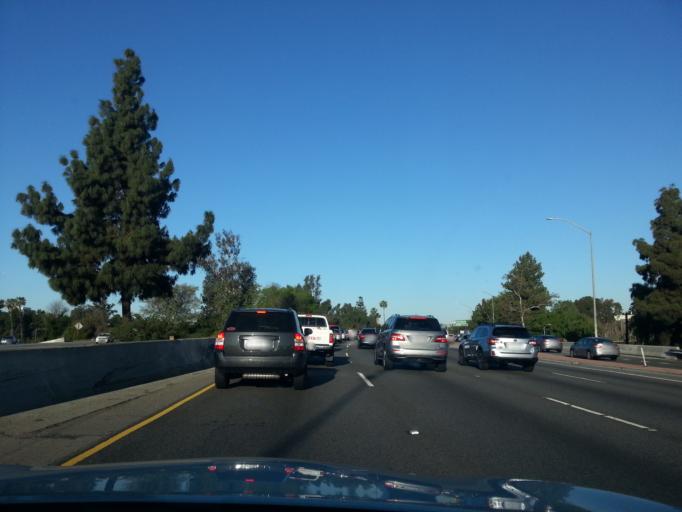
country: US
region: California
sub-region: Los Angeles County
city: Sherman Oaks
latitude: 34.1595
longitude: -118.4654
